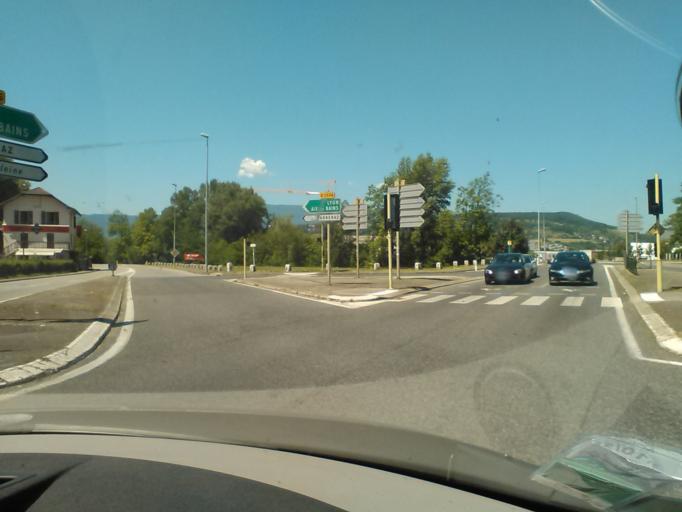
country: FR
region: Rhone-Alpes
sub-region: Departement de la Savoie
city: La Ravoire
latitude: 45.5716
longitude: 5.9599
